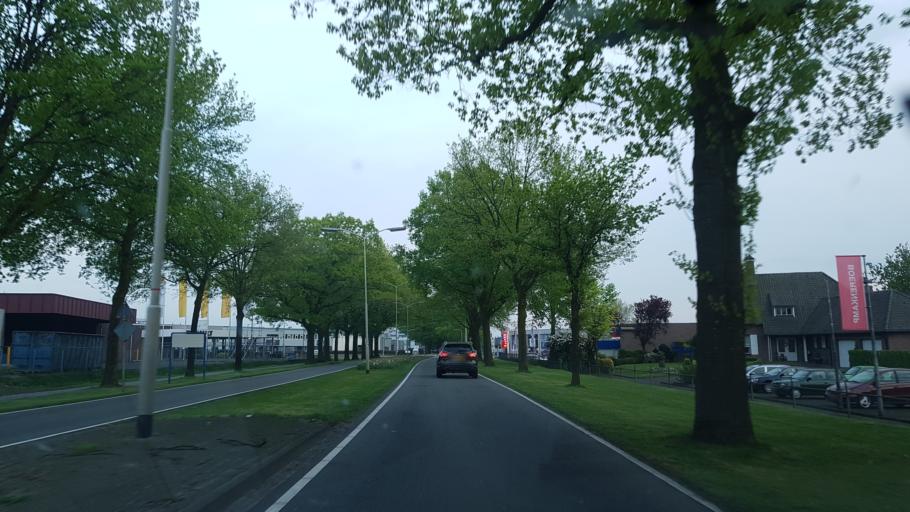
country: NL
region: North Brabant
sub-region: Gemeente Asten
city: Asten
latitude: 51.4516
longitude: 5.7980
